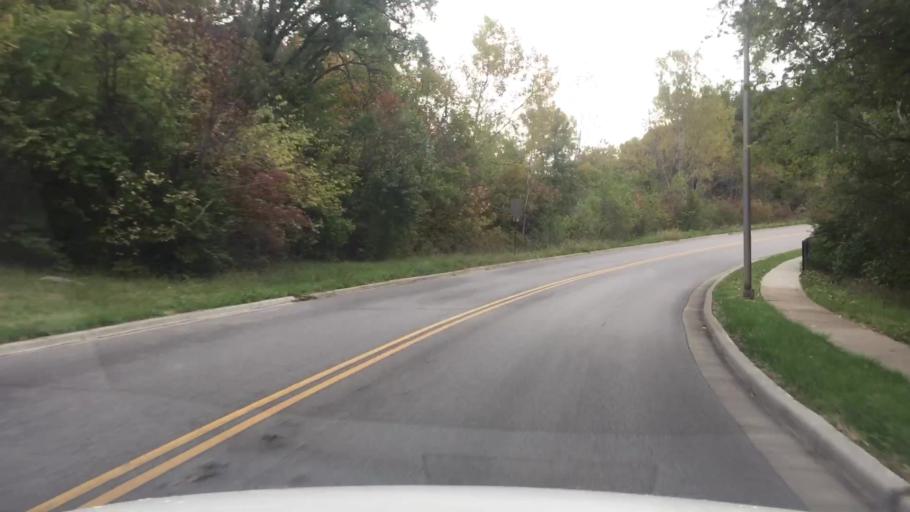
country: US
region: Kansas
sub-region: Johnson County
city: Shawnee
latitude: 39.0244
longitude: -94.7433
